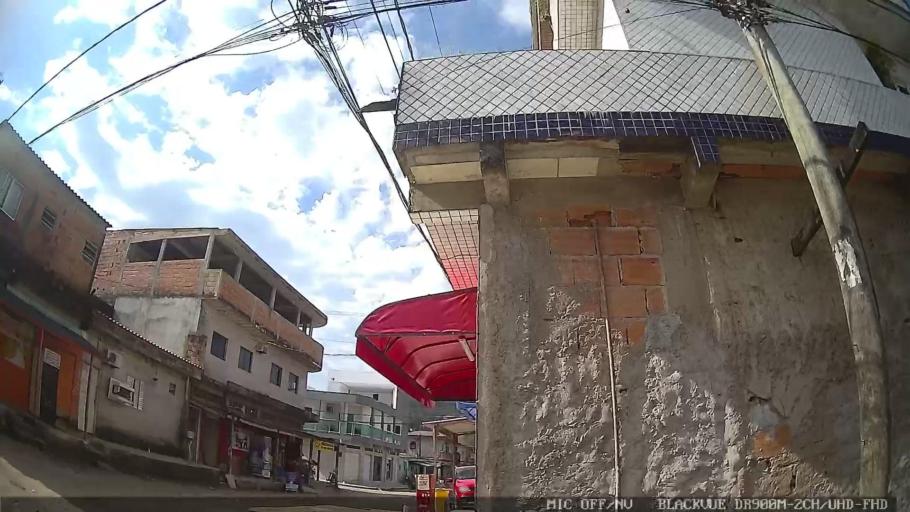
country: BR
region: Sao Paulo
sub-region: Guaruja
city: Guaruja
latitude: -23.9608
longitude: -46.2462
